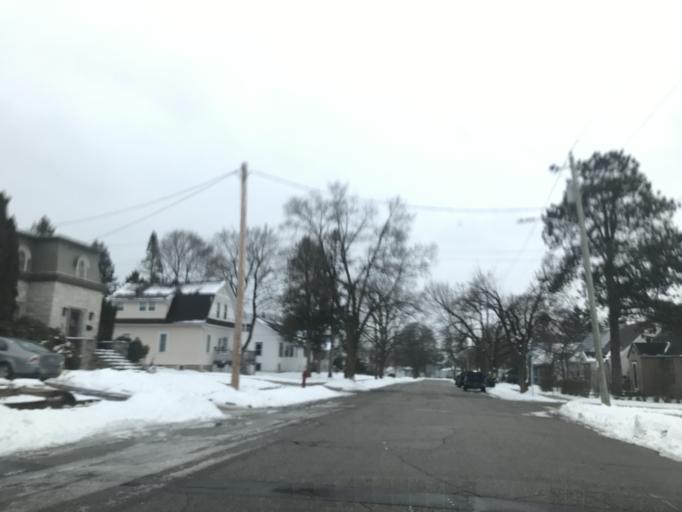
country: US
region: Wisconsin
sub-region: Door County
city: Sturgeon Bay
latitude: 44.8414
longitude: -87.3742
